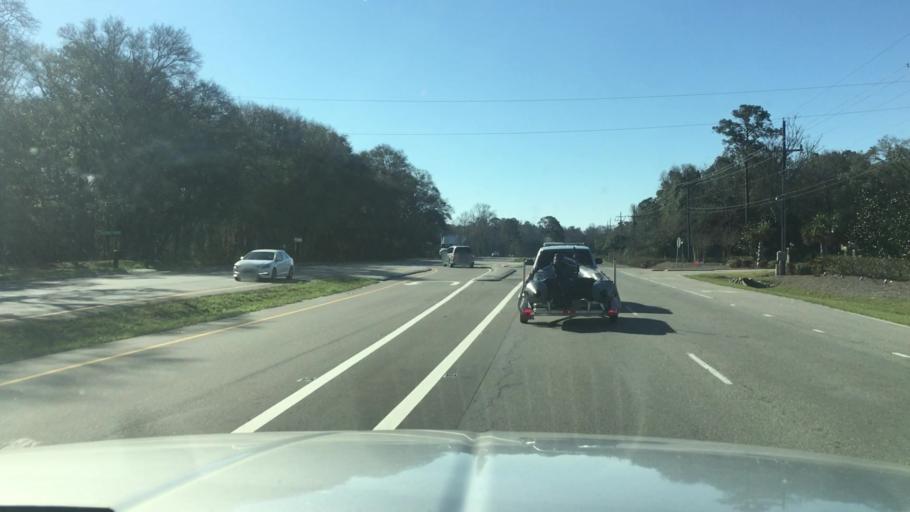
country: US
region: North Carolina
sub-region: New Hanover County
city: Sea Breeze
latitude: 34.0814
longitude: -77.8950
